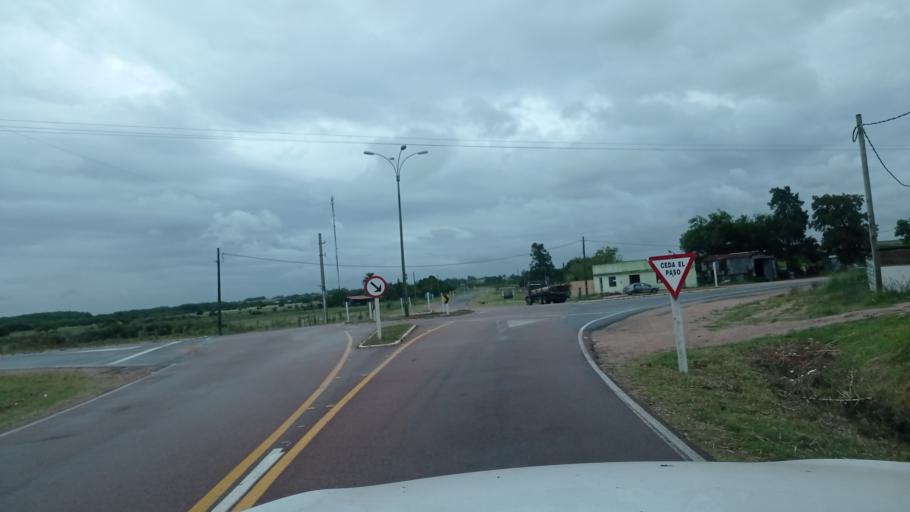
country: UY
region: Canelones
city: Joanico
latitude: -34.5808
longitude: -56.1579
